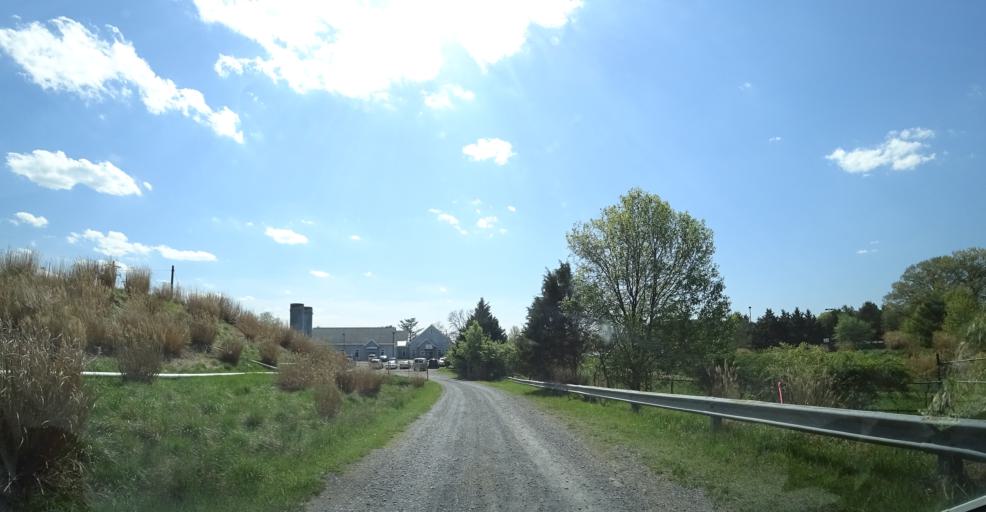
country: US
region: Maryland
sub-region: Montgomery County
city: Derwood
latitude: 39.1075
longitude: -77.1446
